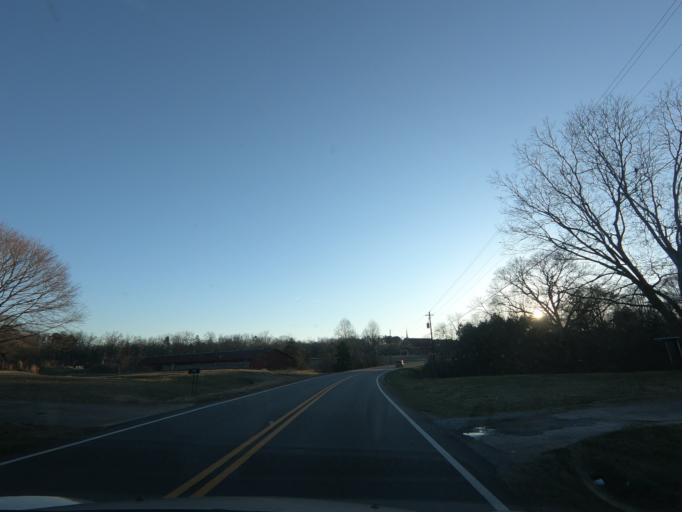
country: US
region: Georgia
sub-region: Dawson County
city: Dawsonville
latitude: 34.3323
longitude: -84.1190
